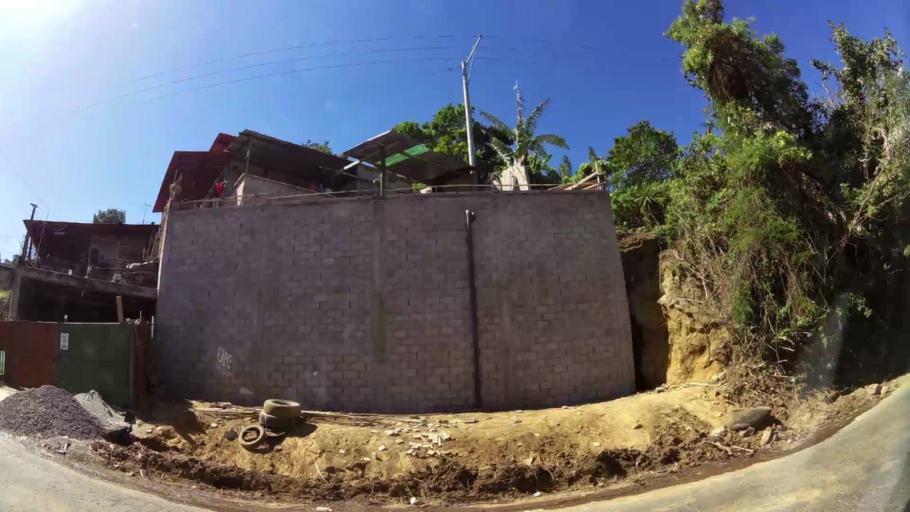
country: SV
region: Ahuachapan
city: Ahuachapan
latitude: 13.9136
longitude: -89.8370
